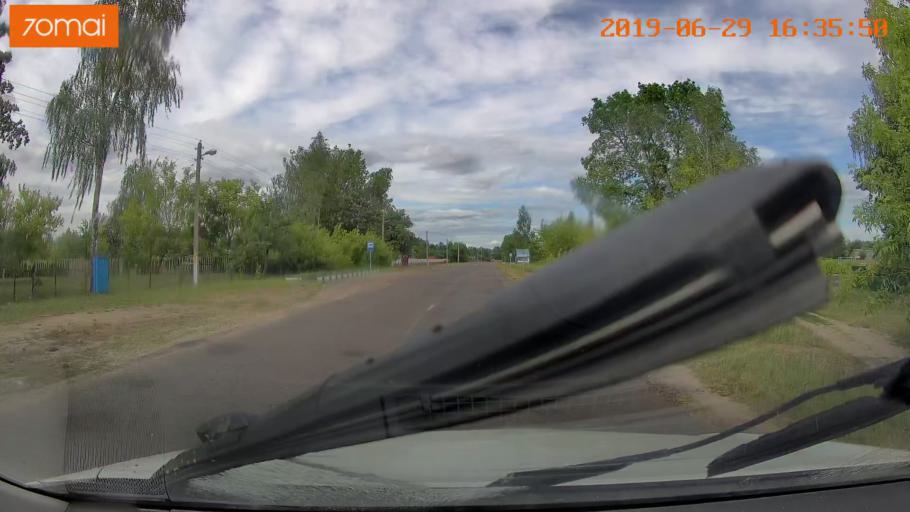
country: BY
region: Brest
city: Luninyets
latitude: 52.2159
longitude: 27.0189
